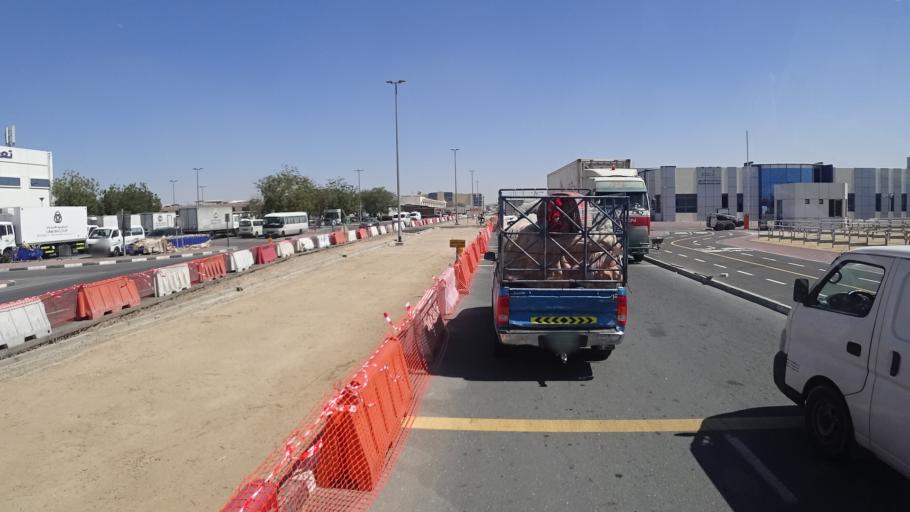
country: AE
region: Ash Shariqah
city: Sharjah
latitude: 25.1745
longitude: 55.3860
